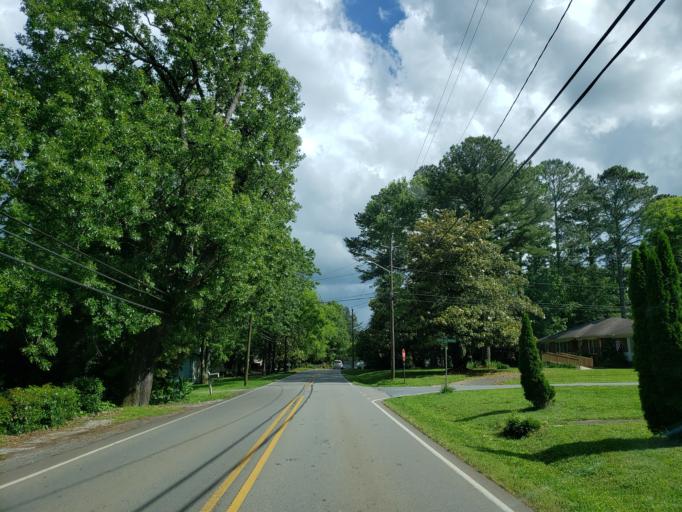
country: US
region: Georgia
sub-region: Pickens County
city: Jasper
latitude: 34.4599
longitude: -84.4285
